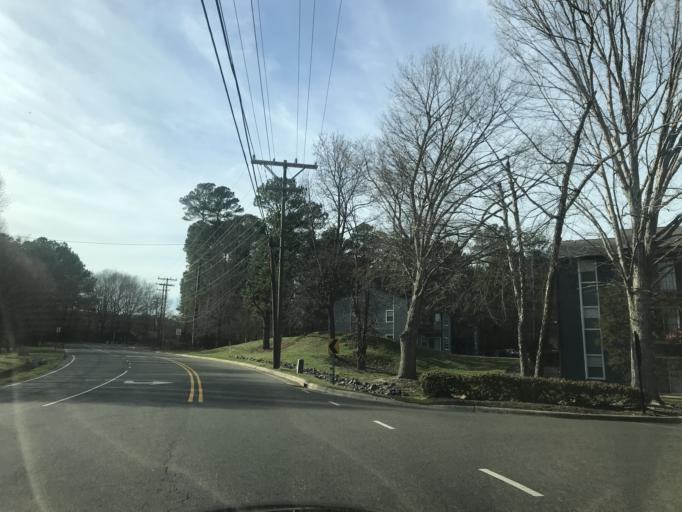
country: US
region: North Carolina
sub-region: Wake County
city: Morrisville
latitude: 35.8915
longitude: -78.8859
